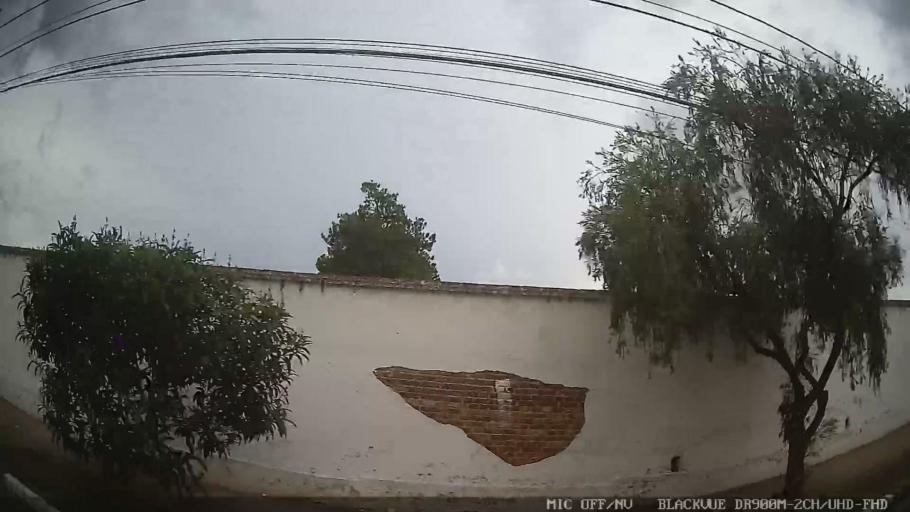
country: BR
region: Sao Paulo
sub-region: Atibaia
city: Atibaia
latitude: -23.1144
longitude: -46.5456
